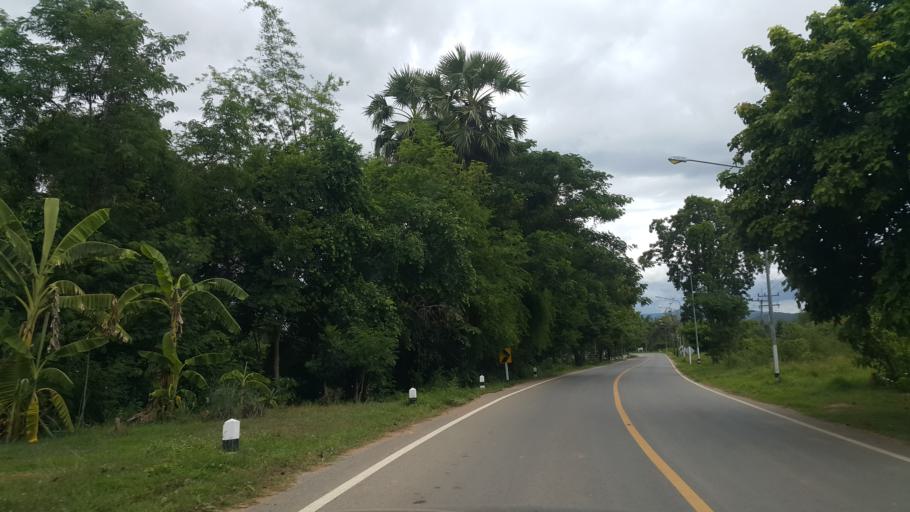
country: TH
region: Sukhothai
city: Ban Na
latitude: 17.0376
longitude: 99.7040
